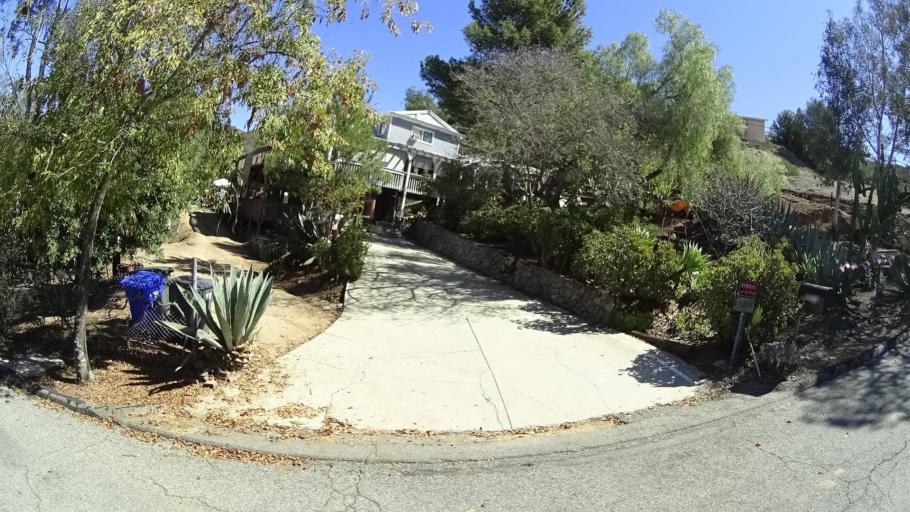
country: US
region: California
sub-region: San Diego County
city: Jamul
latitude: 32.7389
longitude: -116.8708
